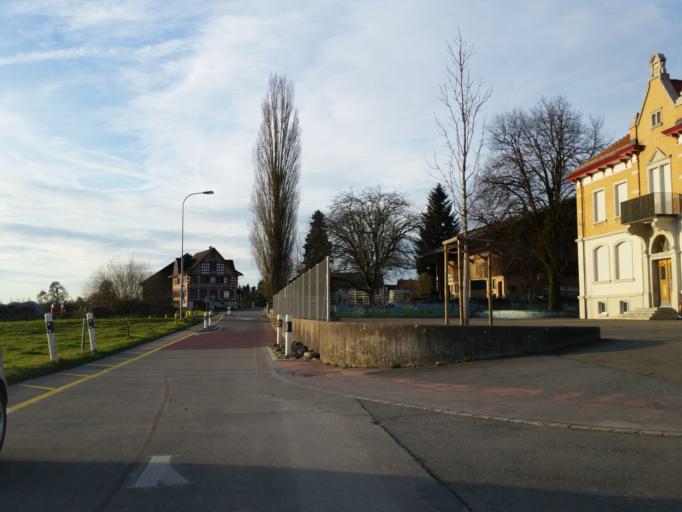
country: CH
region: Thurgau
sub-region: Arbon District
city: Amriswil
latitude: 47.5624
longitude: 9.3147
